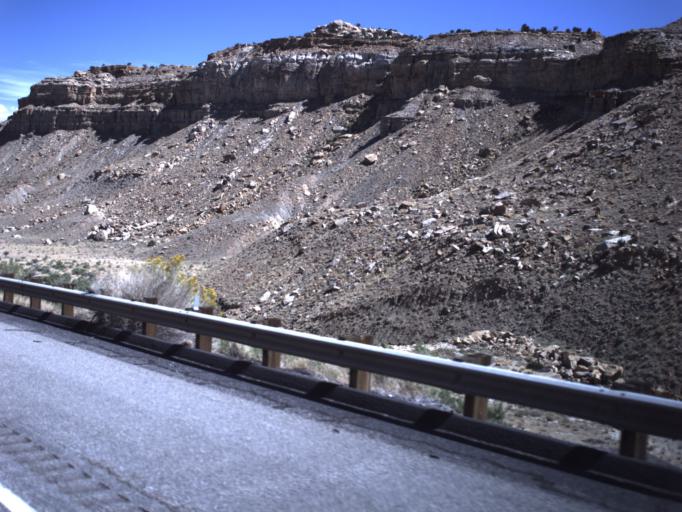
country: US
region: Utah
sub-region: Emery County
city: Ferron
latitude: 38.8058
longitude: -111.2613
